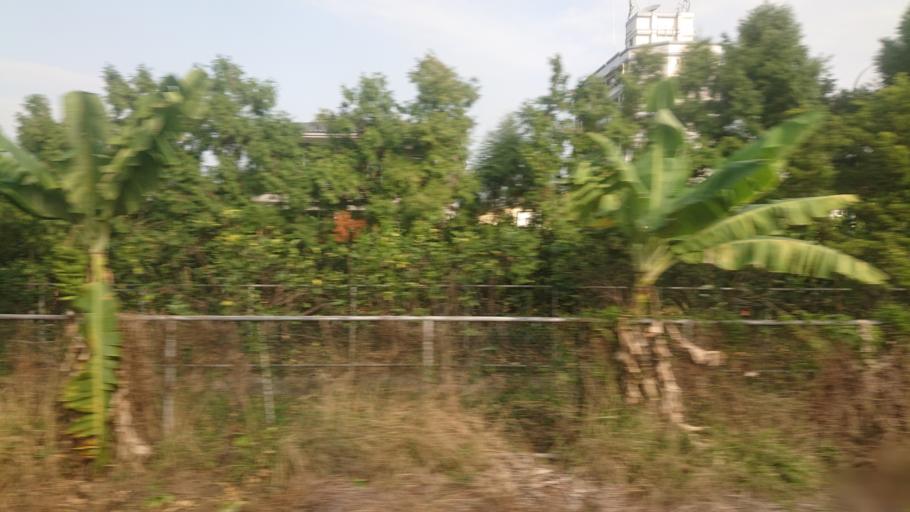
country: TW
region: Taiwan
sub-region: Yunlin
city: Douliu
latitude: 23.7145
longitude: 120.5489
